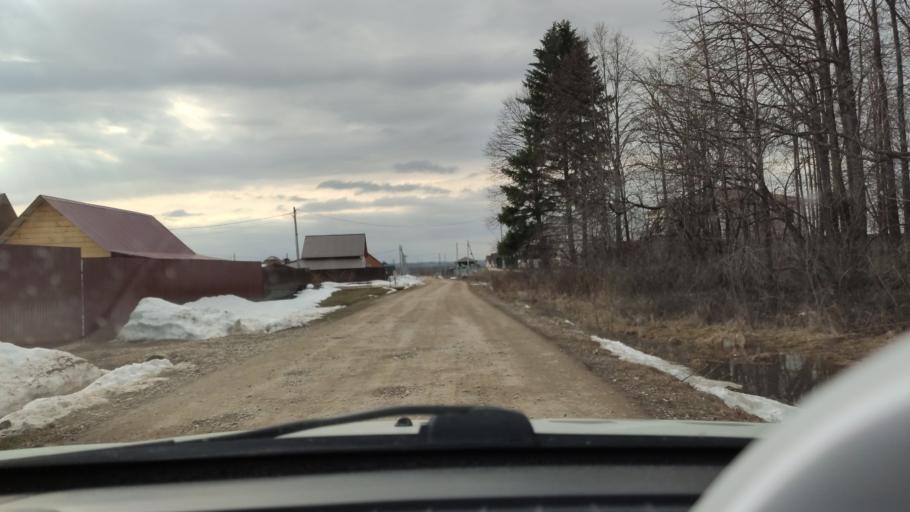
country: RU
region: Perm
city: Ferma
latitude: 57.8843
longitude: 56.3358
